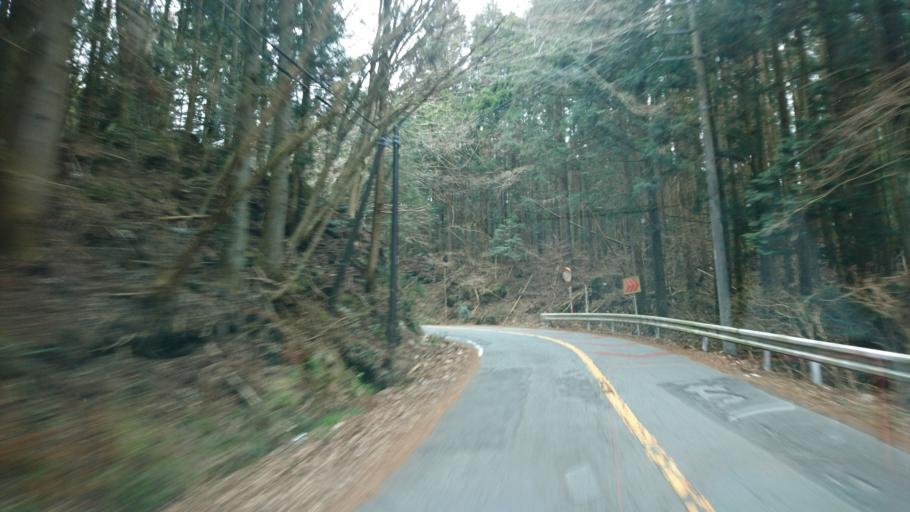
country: JP
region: Shizuoka
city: Fujinomiya
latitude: 35.3490
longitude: 138.5669
